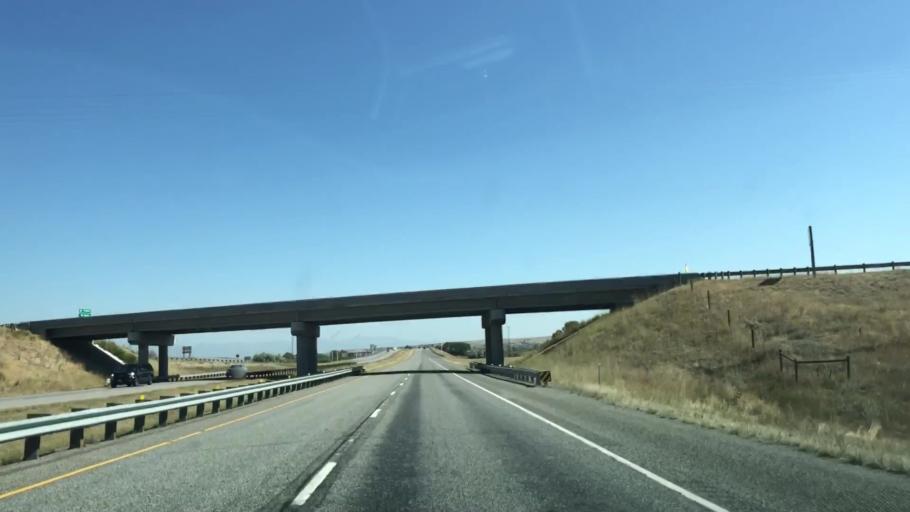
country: US
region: Montana
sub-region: Gallatin County
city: Three Forks
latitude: 45.9018
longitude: -111.5354
